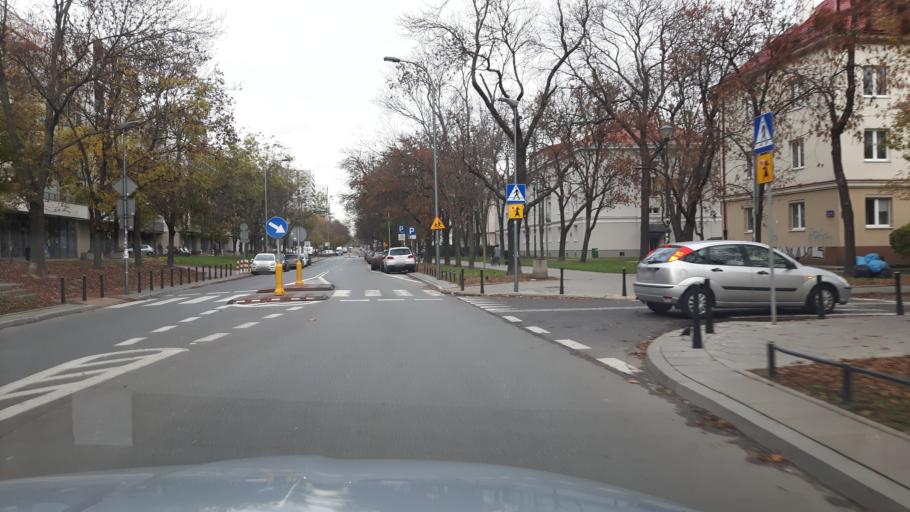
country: PL
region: Masovian Voivodeship
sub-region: Warszawa
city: Mokotow
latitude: 52.1711
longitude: 20.9984
